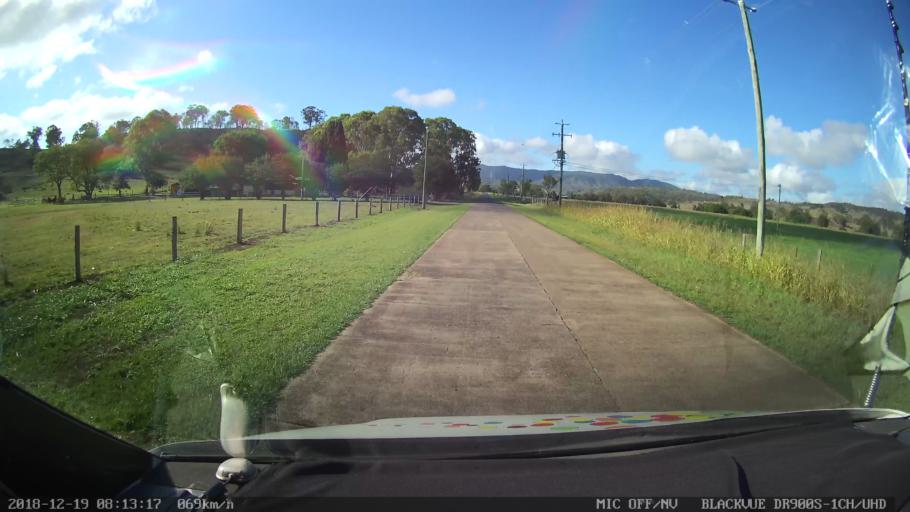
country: AU
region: Queensland
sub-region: Logan
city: Cedar Vale
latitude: -28.2370
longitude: 152.8909
